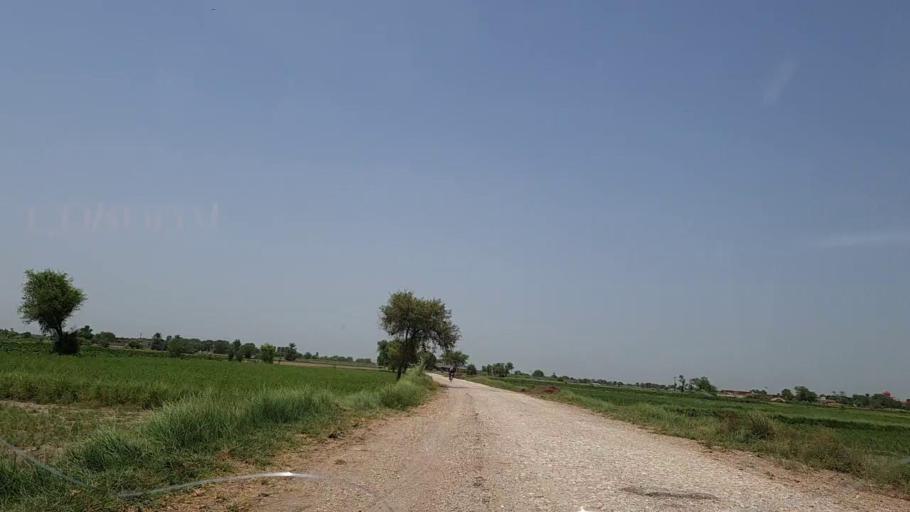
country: PK
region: Sindh
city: Tharu Shah
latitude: 26.9200
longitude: 68.0583
